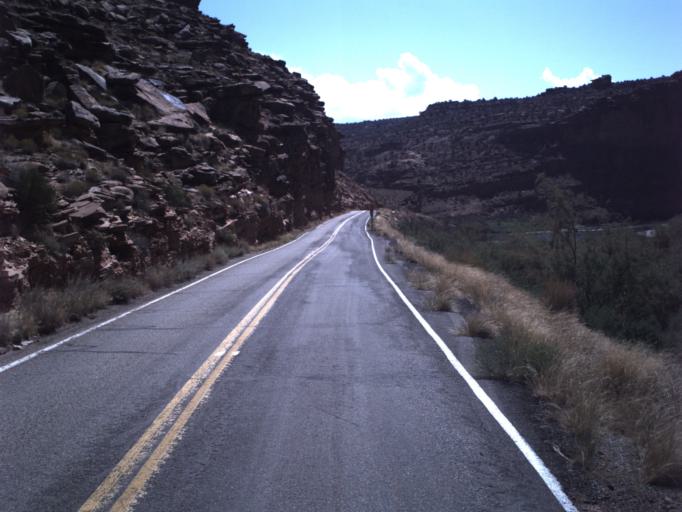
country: US
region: Utah
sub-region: Grand County
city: Moab
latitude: 38.8054
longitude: -109.3132
